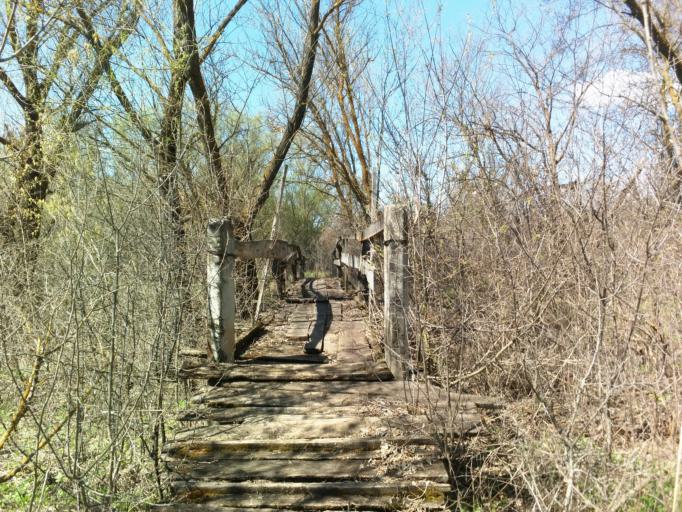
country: RU
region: Voronezj
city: Kalach
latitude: 50.5271
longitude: 40.8054
